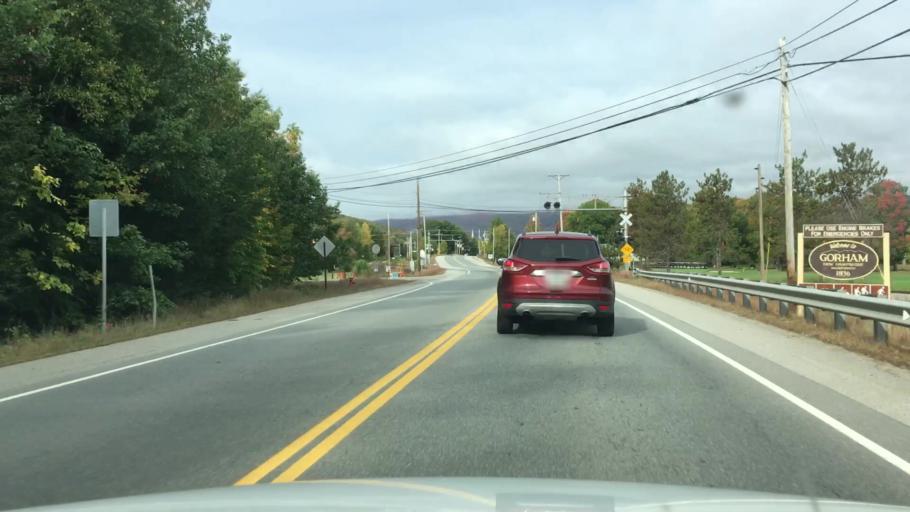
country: US
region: New Hampshire
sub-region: Coos County
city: Gorham
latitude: 44.3856
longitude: -71.1608
